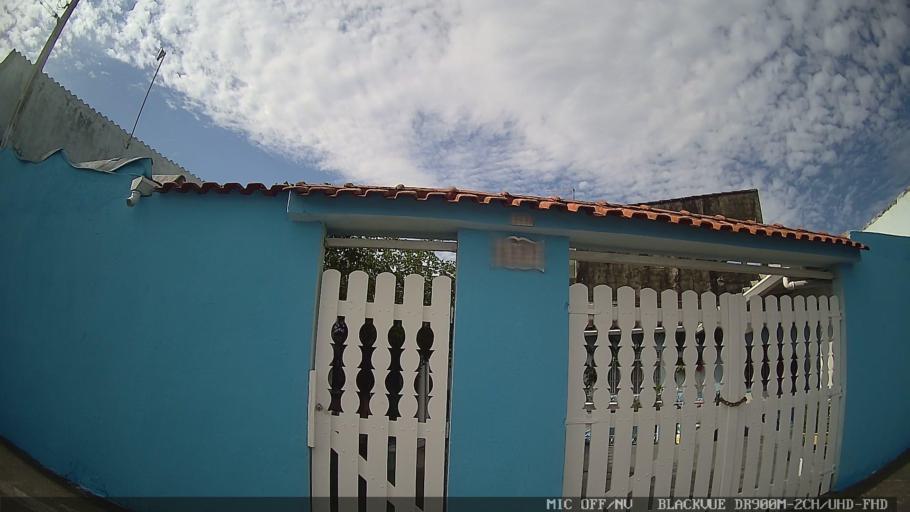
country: BR
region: Sao Paulo
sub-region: Itanhaem
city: Itanhaem
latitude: -24.1605
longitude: -46.7659
